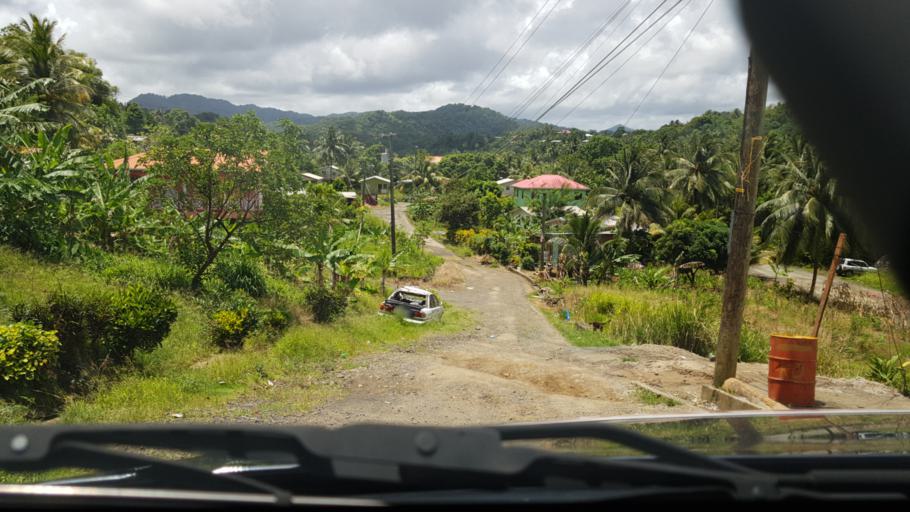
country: LC
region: Anse-la-Raye
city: Anse La Raye
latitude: 13.9519
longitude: -60.9957
